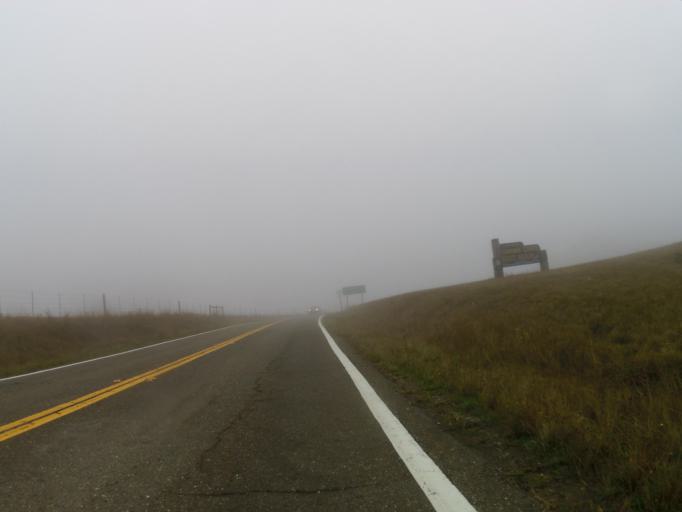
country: US
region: California
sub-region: Sonoma County
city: Monte Rio
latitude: 38.4792
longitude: -123.1652
